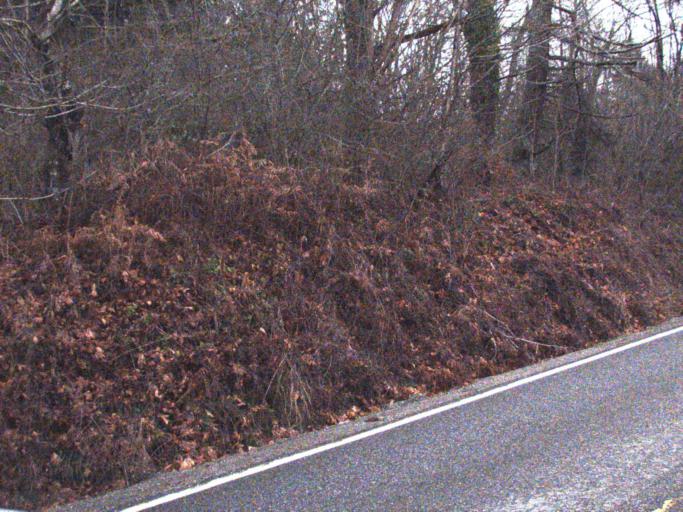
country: US
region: Washington
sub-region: Snohomish County
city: Warm Beach
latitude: 48.1510
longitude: -122.2852
